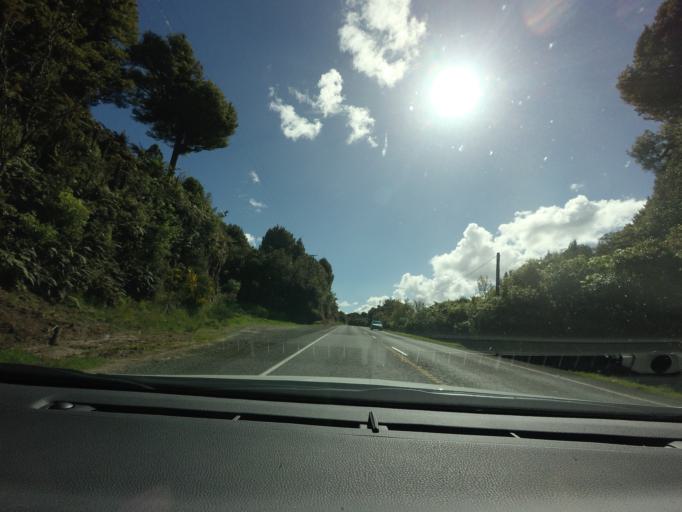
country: NZ
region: Waikato
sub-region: South Waikato District
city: Tokoroa
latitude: -38.0340
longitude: 176.0134
